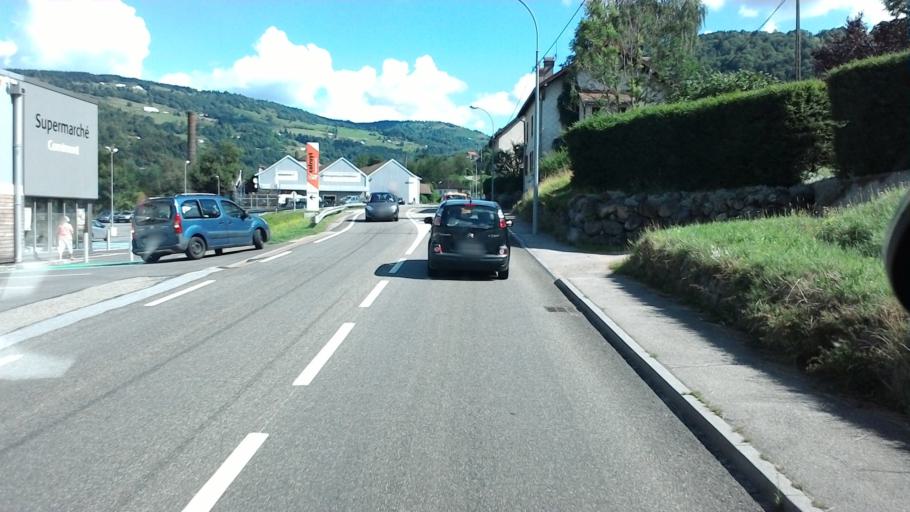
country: FR
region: Lorraine
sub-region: Departement des Vosges
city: Cornimont
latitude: 47.9675
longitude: 6.8332
